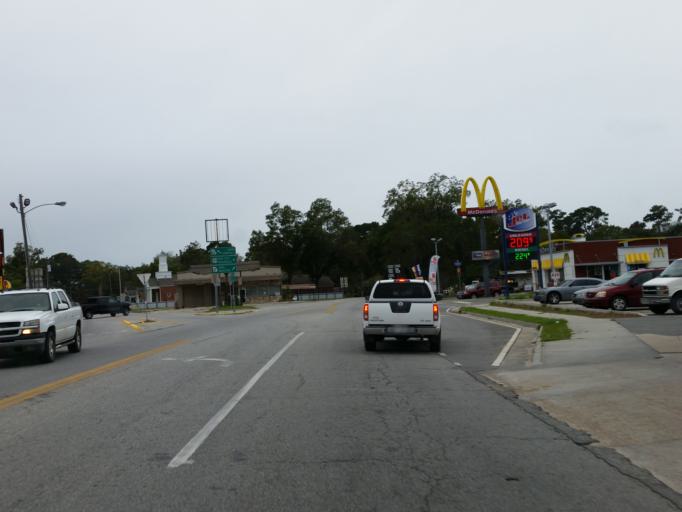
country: US
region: Georgia
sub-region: Lanier County
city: Lakeland
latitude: 31.0410
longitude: -83.0762
